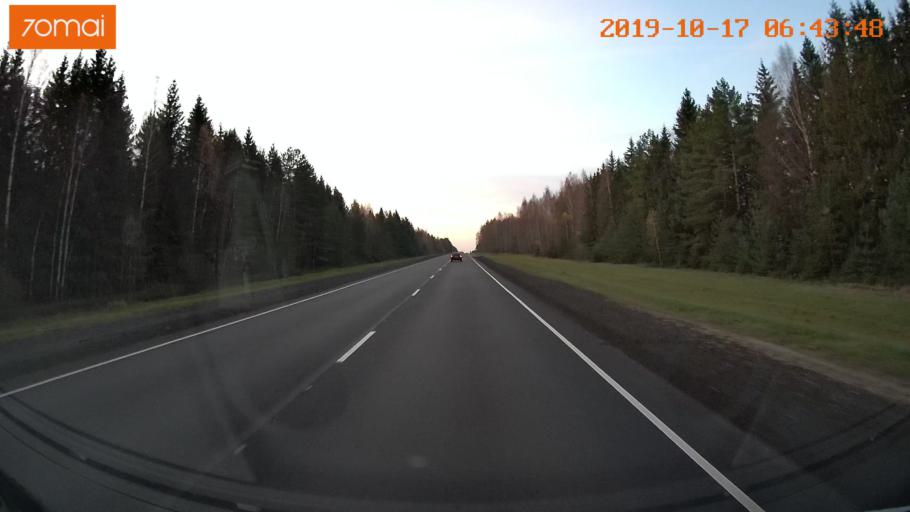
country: RU
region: Vladimir
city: Kideksha
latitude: 56.5820
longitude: 40.5549
